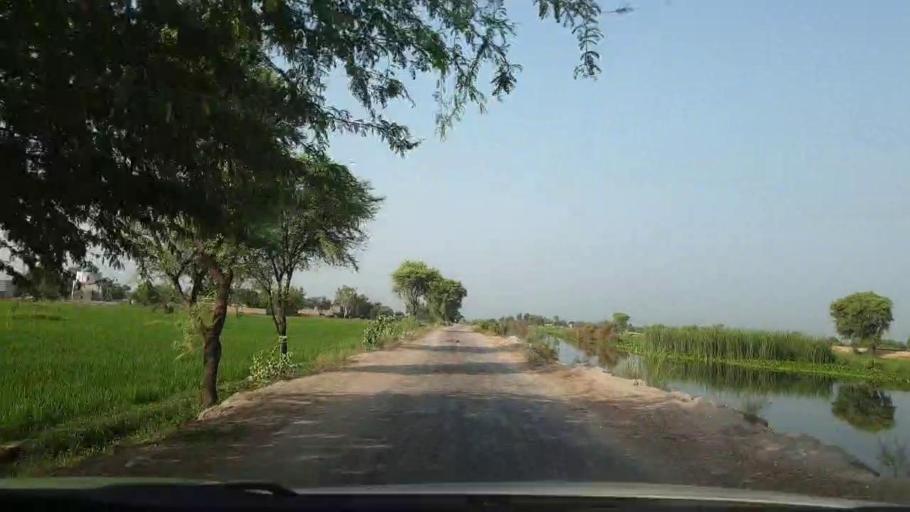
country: PK
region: Sindh
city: Larkana
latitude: 27.5074
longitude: 68.1808
